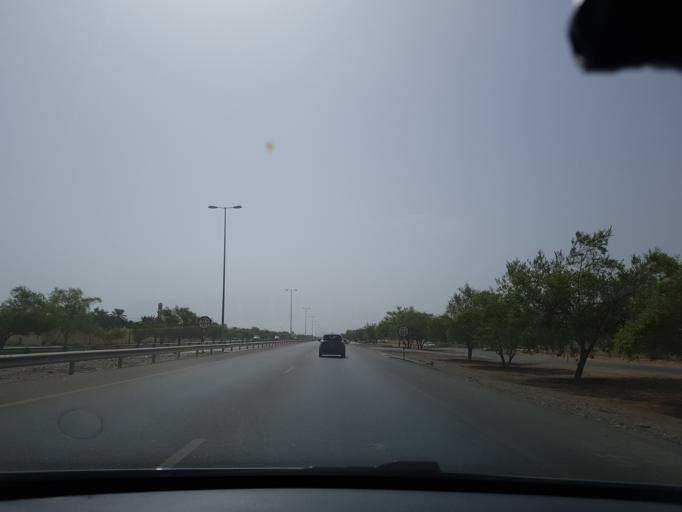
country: OM
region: Al Batinah
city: Al Khaburah
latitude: 23.9411
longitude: 57.1236
